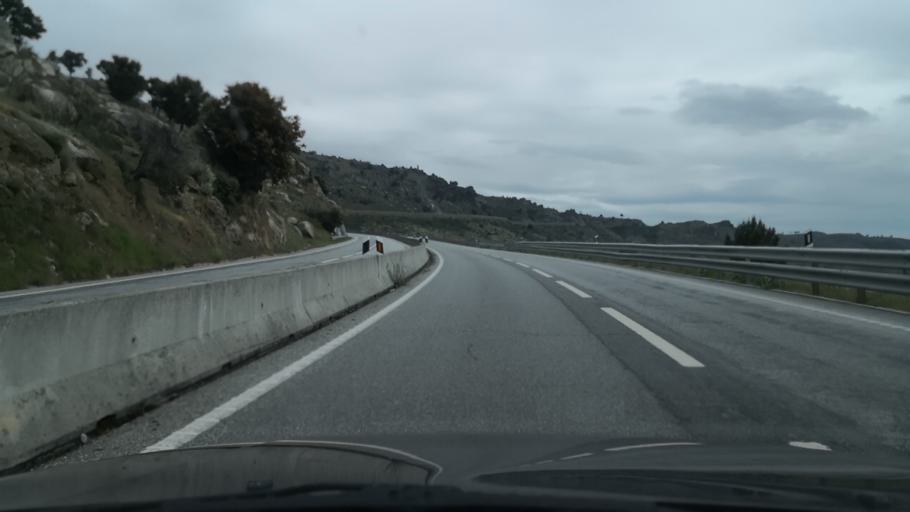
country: PT
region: Guarda
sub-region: Guarda
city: Guarda
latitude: 40.6037
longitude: -7.2823
